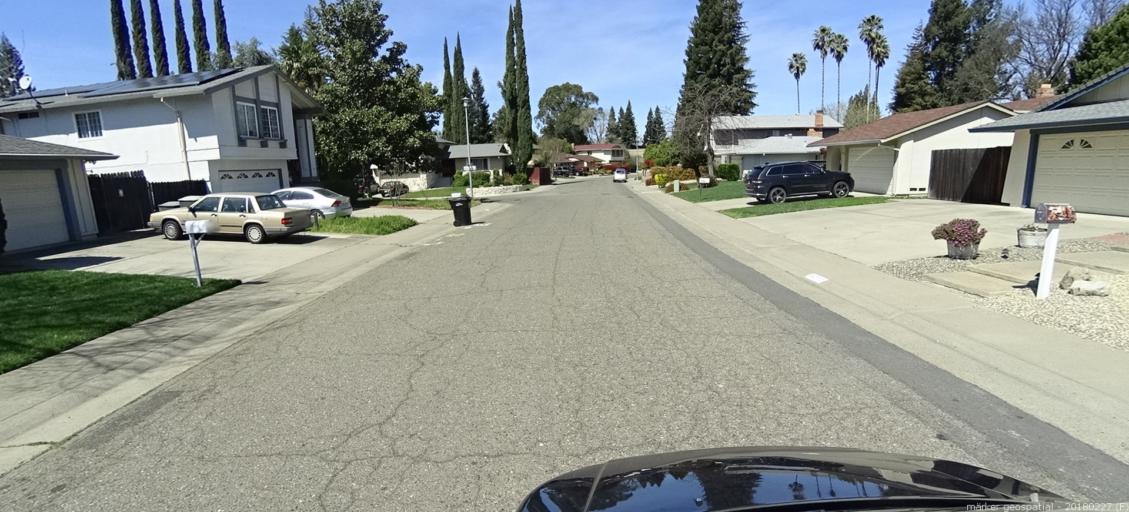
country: US
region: California
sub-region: Sacramento County
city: La Riviera
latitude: 38.5596
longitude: -121.3523
